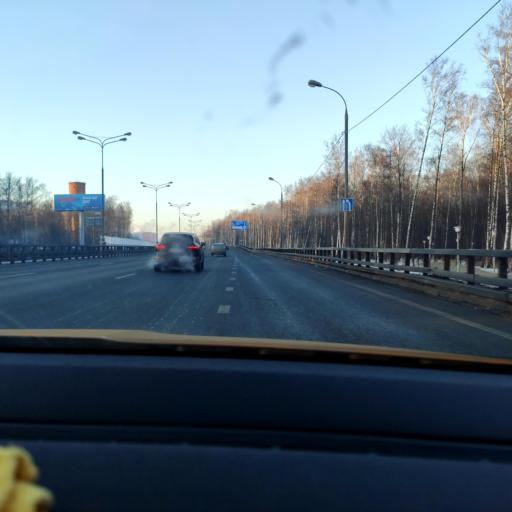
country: RU
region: Moscow
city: Novo-Peredelkino
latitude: 55.6316
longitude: 37.3211
